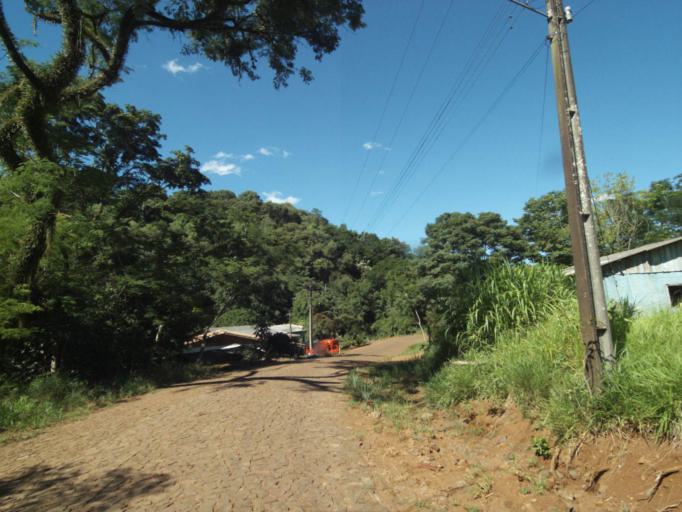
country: BR
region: Parana
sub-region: Ampere
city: Ampere
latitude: -26.1684
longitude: -53.3680
